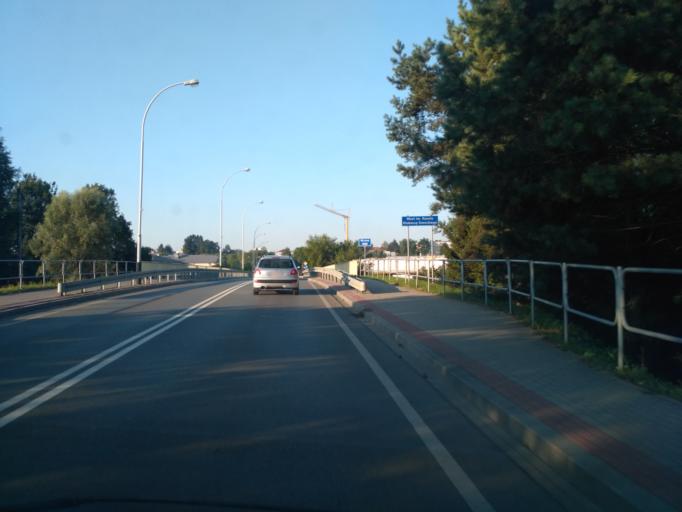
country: PL
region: Subcarpathian Voivodeship
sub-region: Krosno
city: Krosno
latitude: 49.6946
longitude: 21.7740
